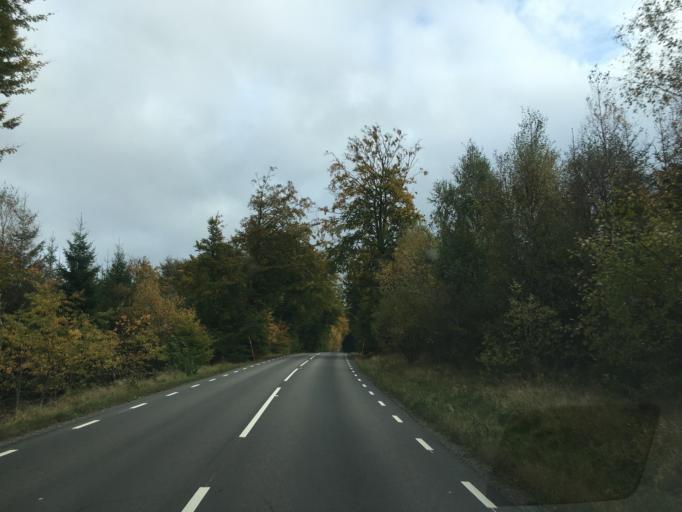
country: SE
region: Skane
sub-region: Tomelilla Kommun
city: Tomelilla
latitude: 55.6349
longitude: 14.0877
